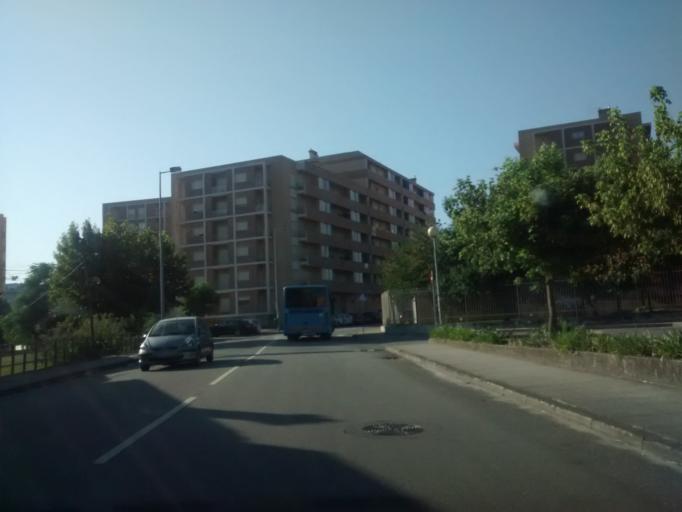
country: PT
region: Braga
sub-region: Braga
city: Braga
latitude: 41.5468
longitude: -8.4029
